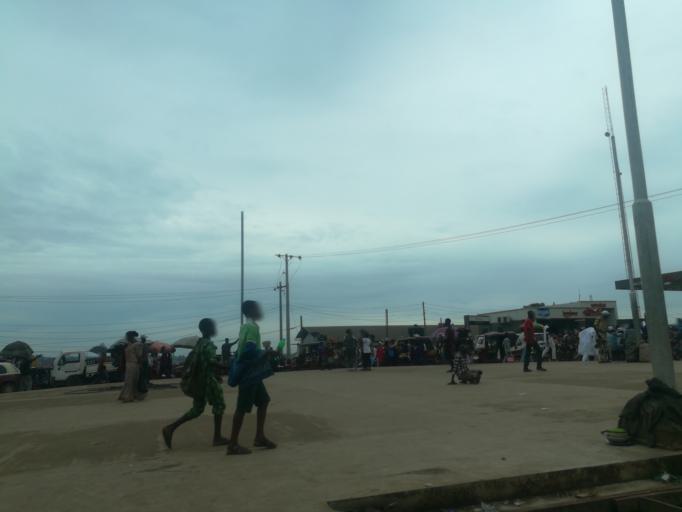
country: NG
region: Oyo
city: Ibadan
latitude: 7.3971
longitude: 3.9200
